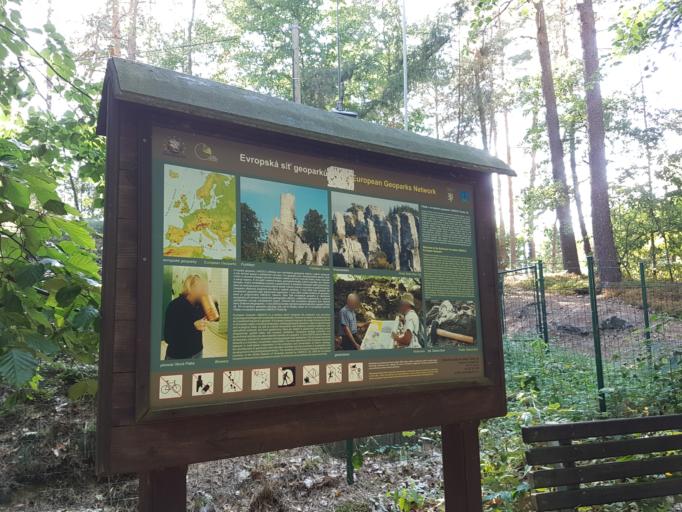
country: CZ
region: Liberecky
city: Mala Skala
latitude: 50.6278
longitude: 15.2069
